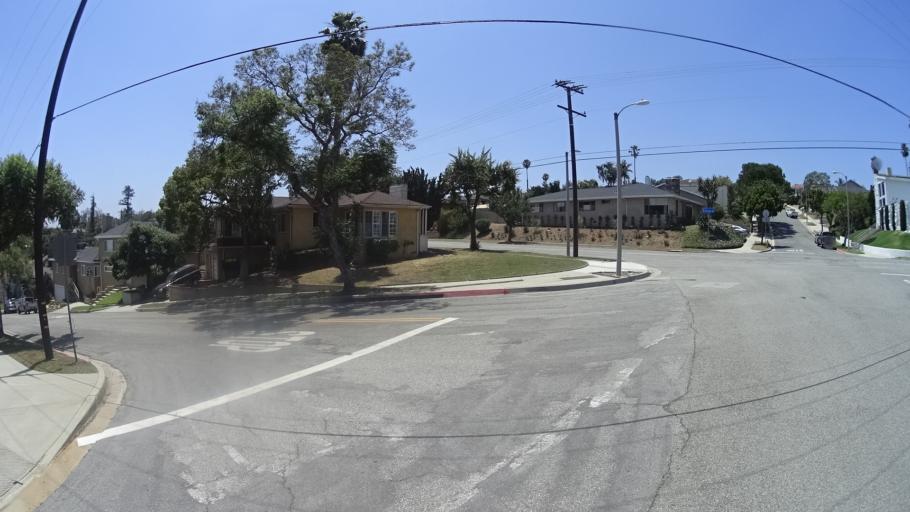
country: US
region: California
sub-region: Los Angeles County
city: View Park-Windsor Hills
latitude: 33.9962
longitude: -118.3527
